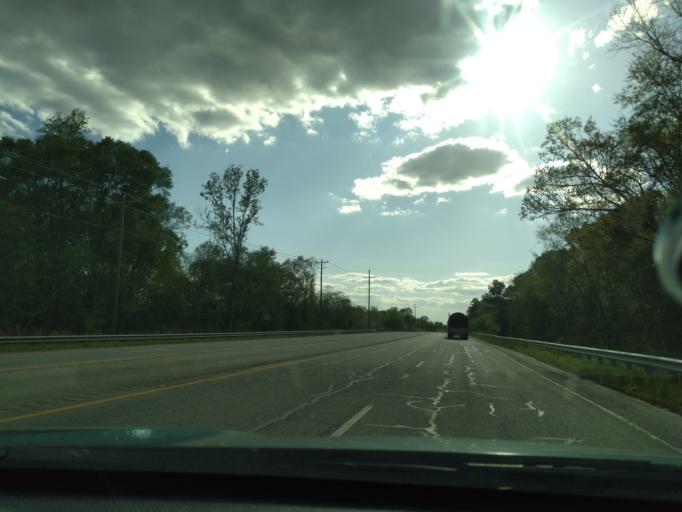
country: US
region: South Carolina
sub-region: Williamsburg County
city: Kingstree
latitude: 33.6618
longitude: -79.8388
